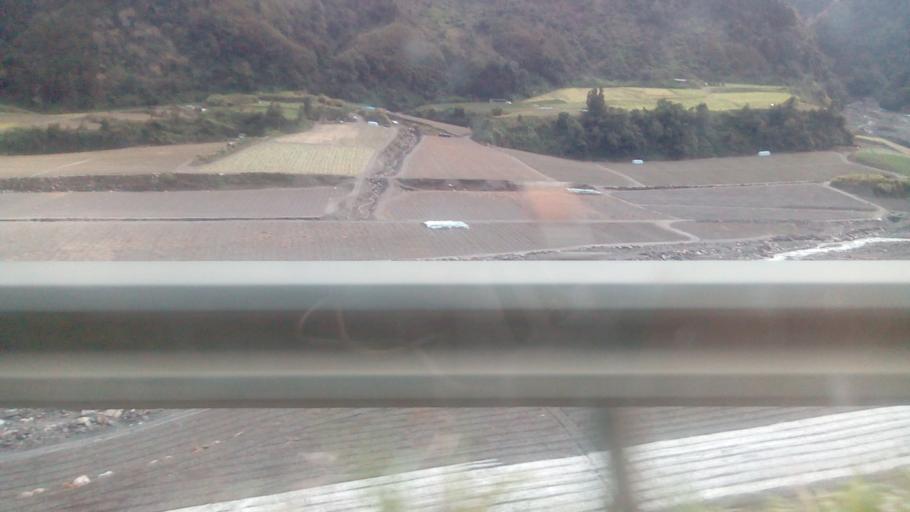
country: TW
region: Taiwan
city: Daxi
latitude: 24.4531
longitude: 121.3910
